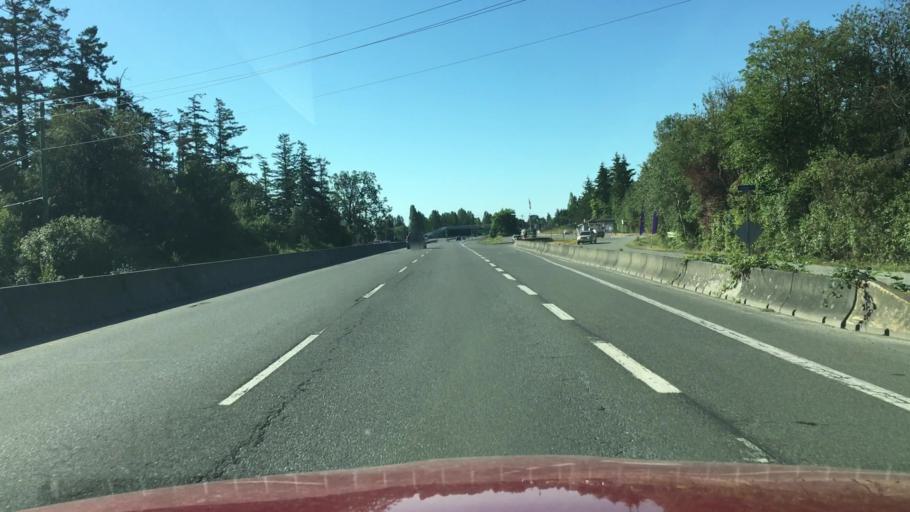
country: CA
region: British Columbia
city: North Saanich
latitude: 48.6664
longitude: -123.4215
